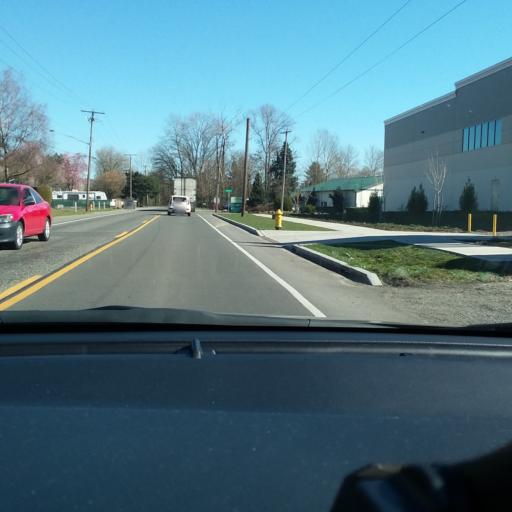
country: US
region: Washington
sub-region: Pierce County
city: Sumner
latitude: 47.2041
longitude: -122.2612
